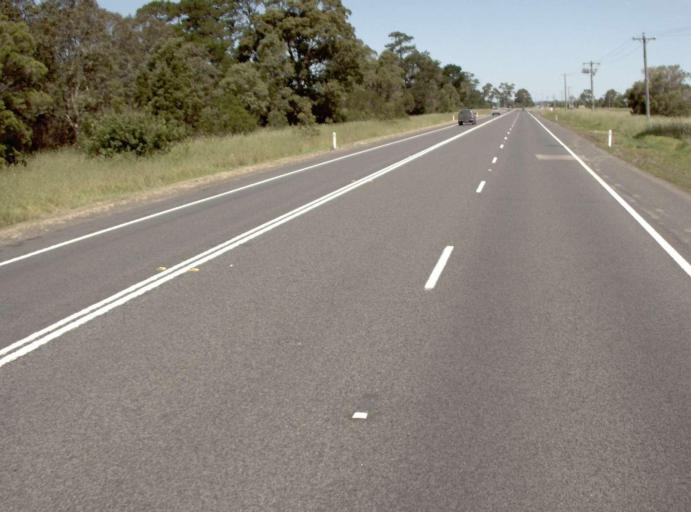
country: AU
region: Victoria
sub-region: Wellington
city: Sale
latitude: -38.0615
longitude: 147.0709
